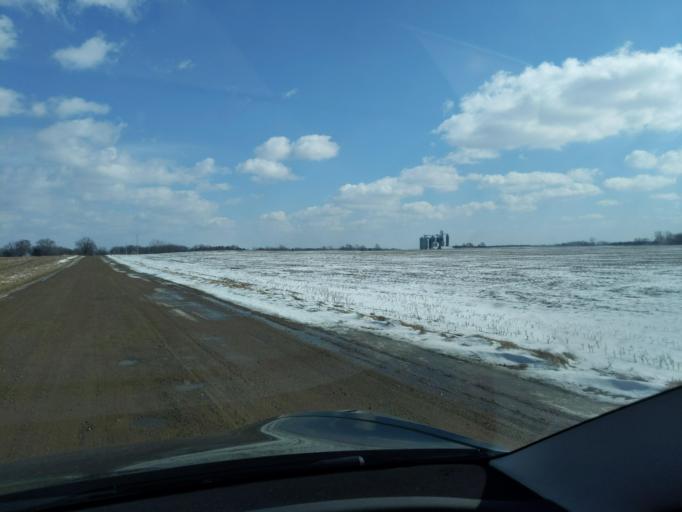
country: US
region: Michigan
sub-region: Ingham County
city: Webberville
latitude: 42.6154
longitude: -84.2331
